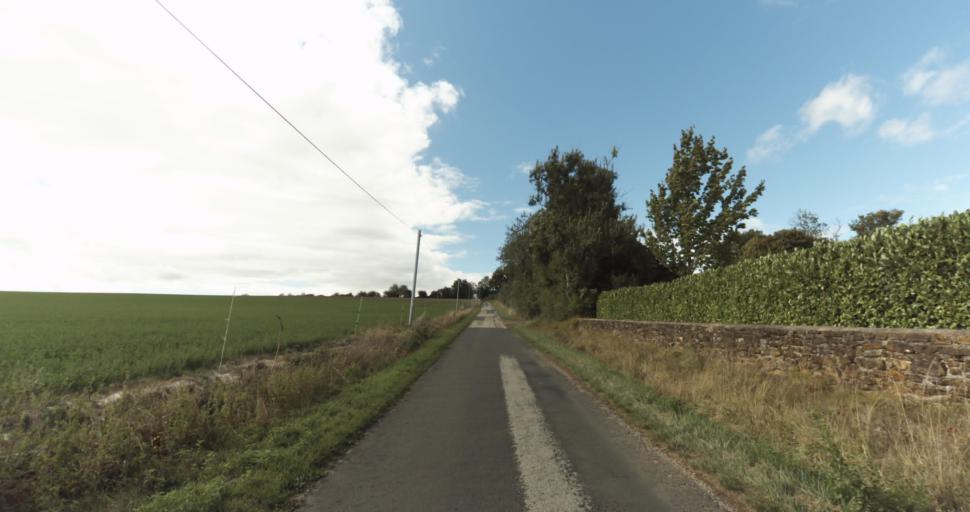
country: FR
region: Lower Normandy
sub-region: Departement de l'Orne
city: Gace
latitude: 48.7736
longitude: 0.3395
